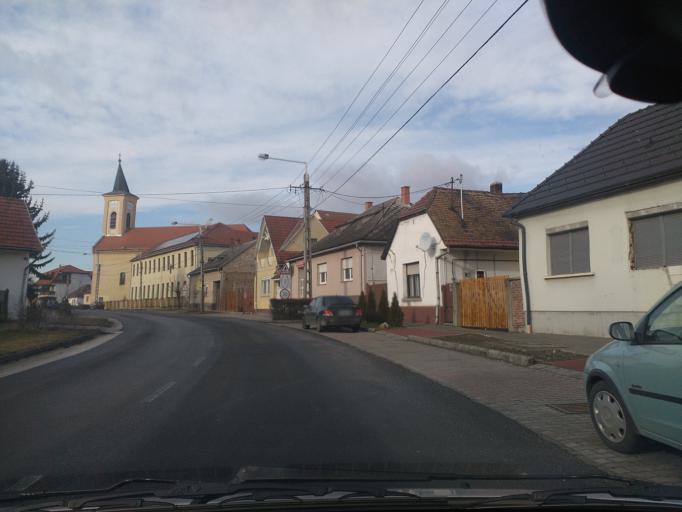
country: HU
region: Komarom-Esztergom
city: Tat
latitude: 47.7447
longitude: 18.6456
